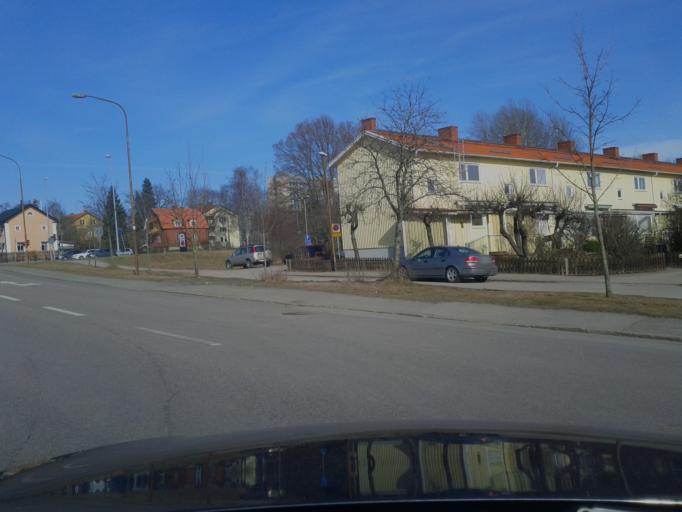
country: SE
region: Vaestmanland
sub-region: Vasteras
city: Vasteras
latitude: 59.6144
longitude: 16.5768
